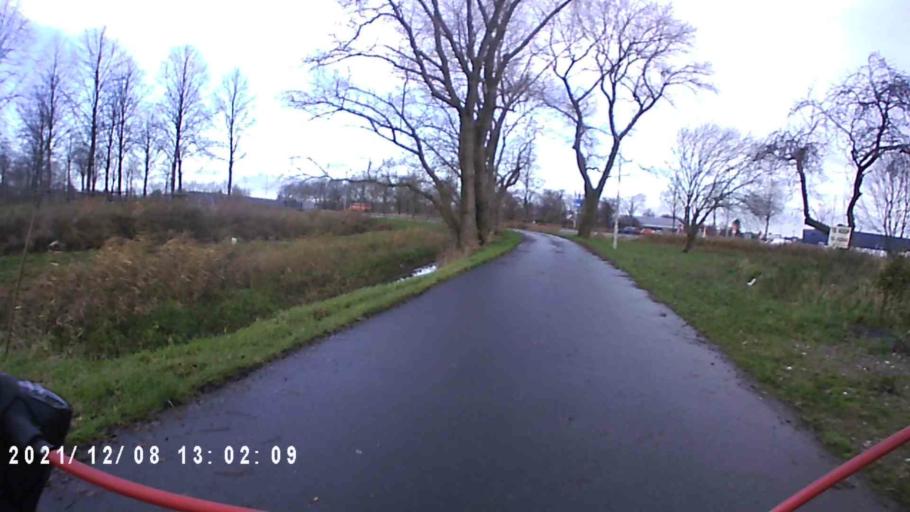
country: NL
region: Groningen
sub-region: Gemeente Haren
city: Haren
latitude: 53.2044
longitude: 6.6252
